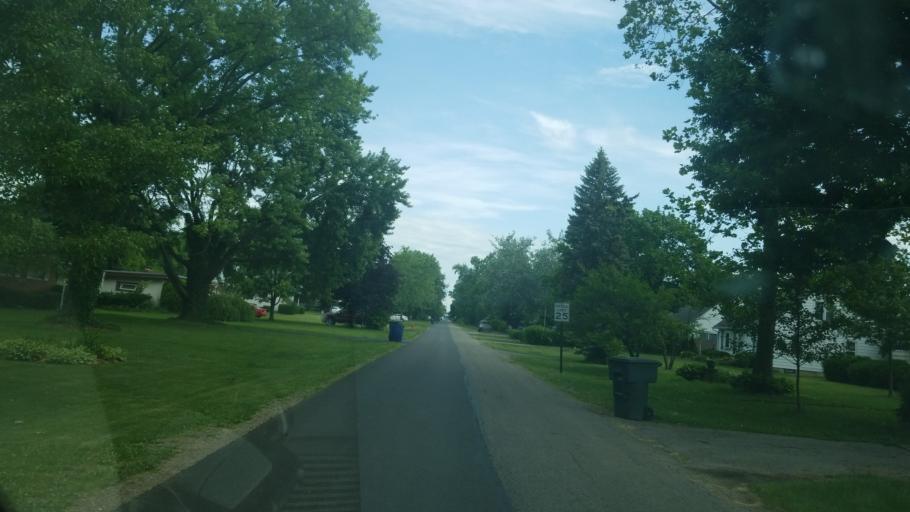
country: US
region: Ohio
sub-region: Franklin County
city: Worthington
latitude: 40.0555
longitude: -82.9946
